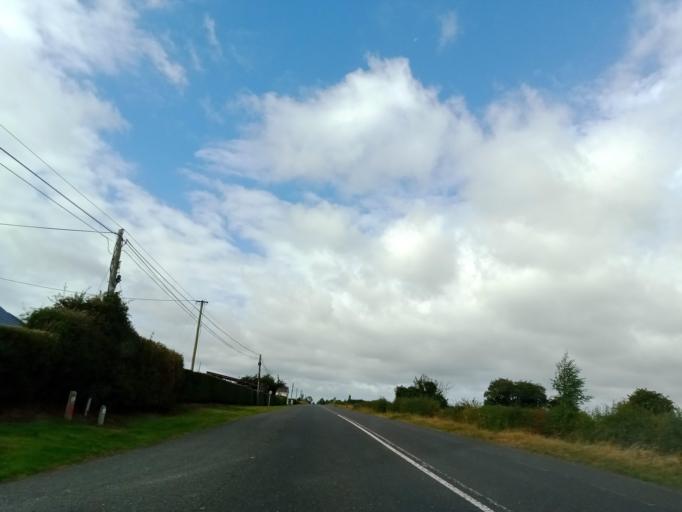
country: IE
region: Leinster
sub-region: Laois
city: Abbeyleix
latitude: 52.8290
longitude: -7.4552
